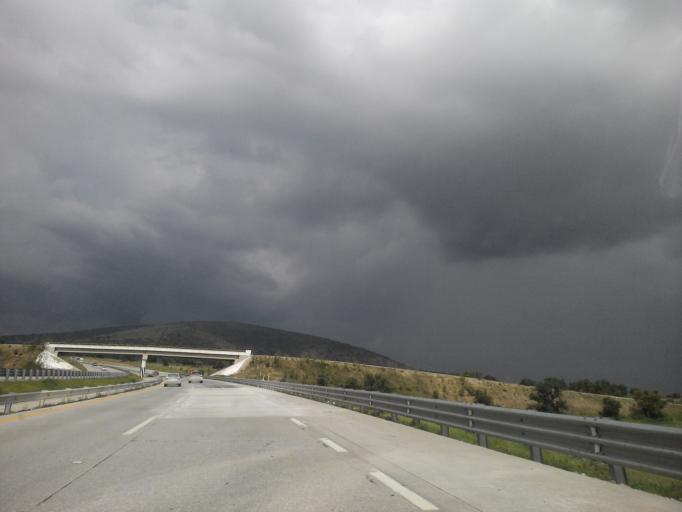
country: MX
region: Mexico
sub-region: Hueypoxtla
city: Santa Maria Ajoloapan
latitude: 19.9548
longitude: -99.0483
